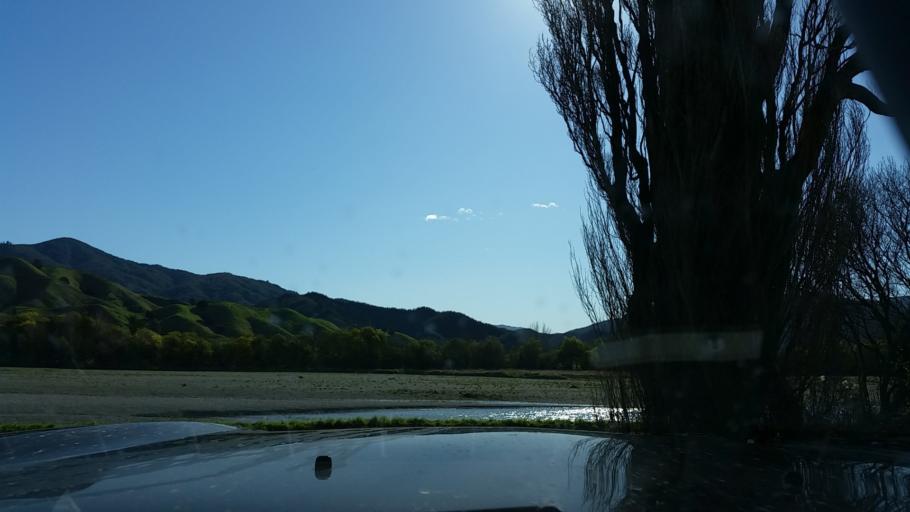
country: NZ
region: Marlborough
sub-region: Marlborough District
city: Blenheim
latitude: -41.4411
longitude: 173.9480
